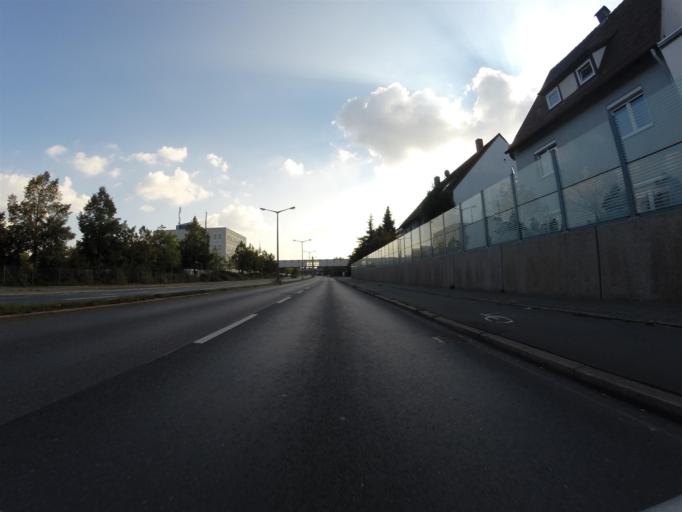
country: DE
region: Bavaria
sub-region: Regierungsbezirk Mittelfranken
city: Grossreuth bei Schweinau
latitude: 49.4481
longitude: 11.0362
